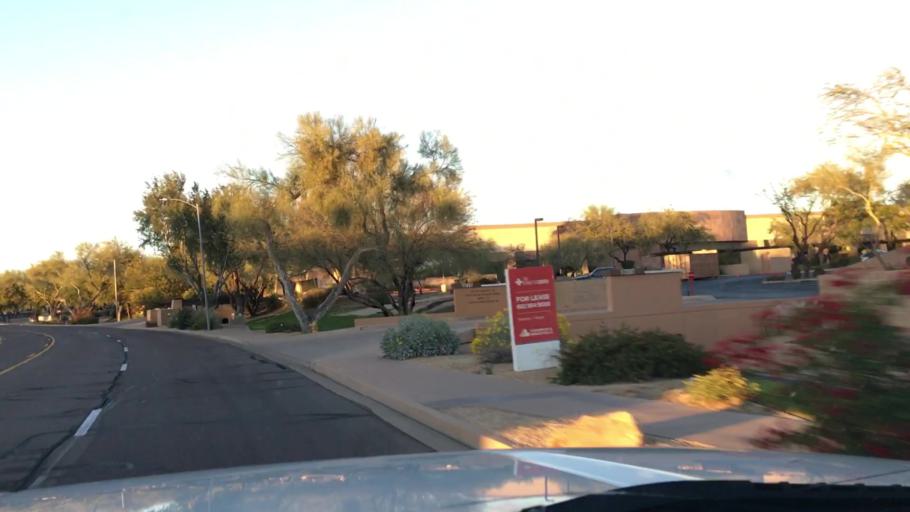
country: US
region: Arizona
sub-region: Maricopa County
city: Paradise Valley
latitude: 33.6418
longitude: -111.8967
